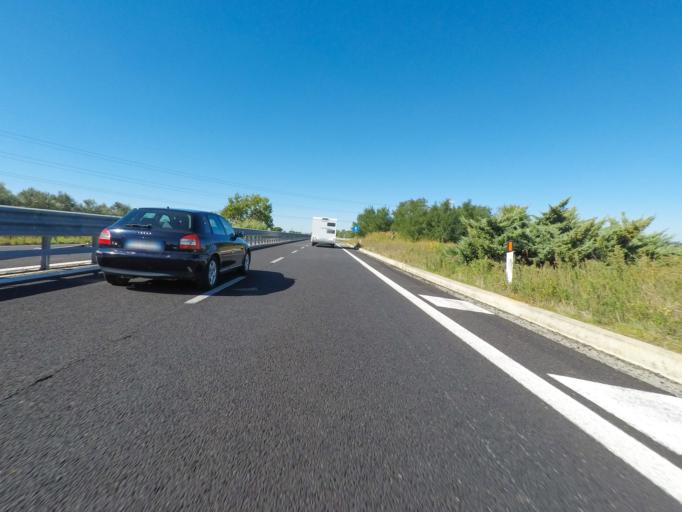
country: IT
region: Latium
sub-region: Provincia di Viterbo
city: Tarquinia
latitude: 42.2776
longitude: 11.7020
